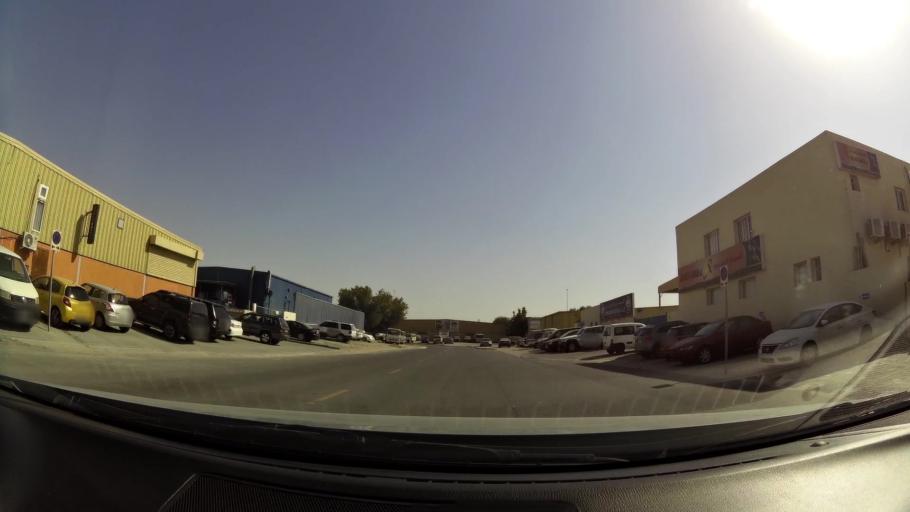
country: AE
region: Dubai
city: Dubai
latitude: 25.1174
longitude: 55.2144
